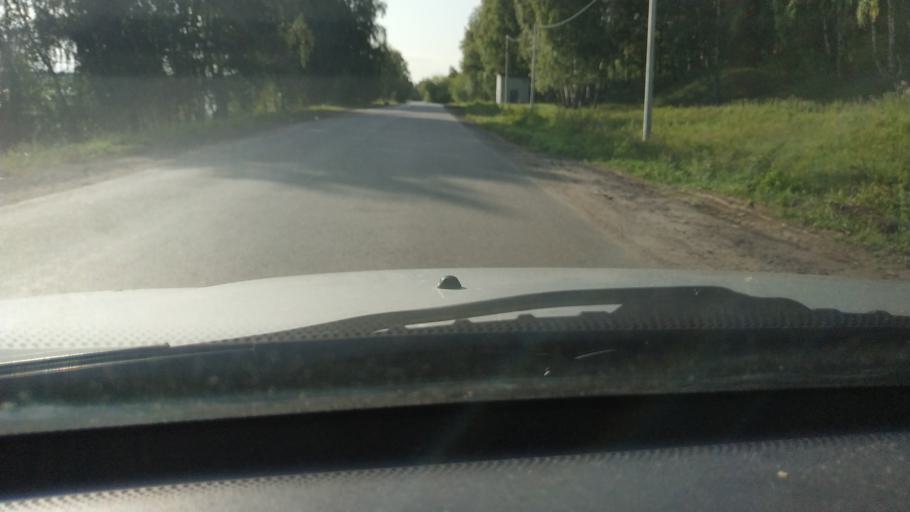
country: RU
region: Kostroma
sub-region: Kostromskoy Rayon
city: Kostroma
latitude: 57.7535
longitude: 40.9224
